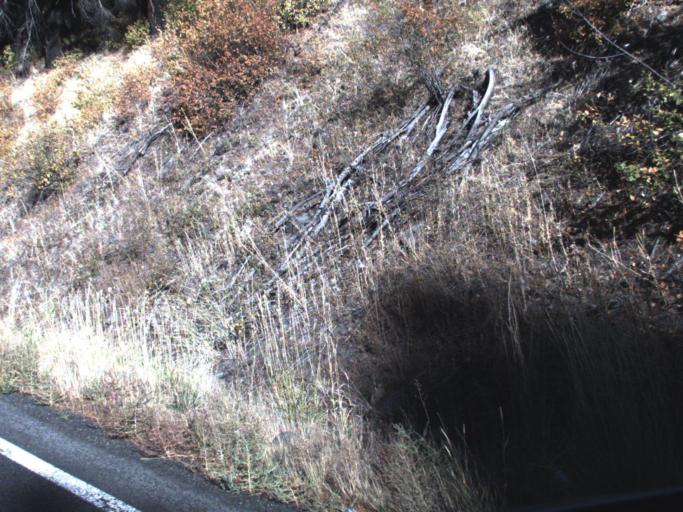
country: US
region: Washington
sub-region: Yakima County
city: Tieton
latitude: 46.6757
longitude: -121.0638
